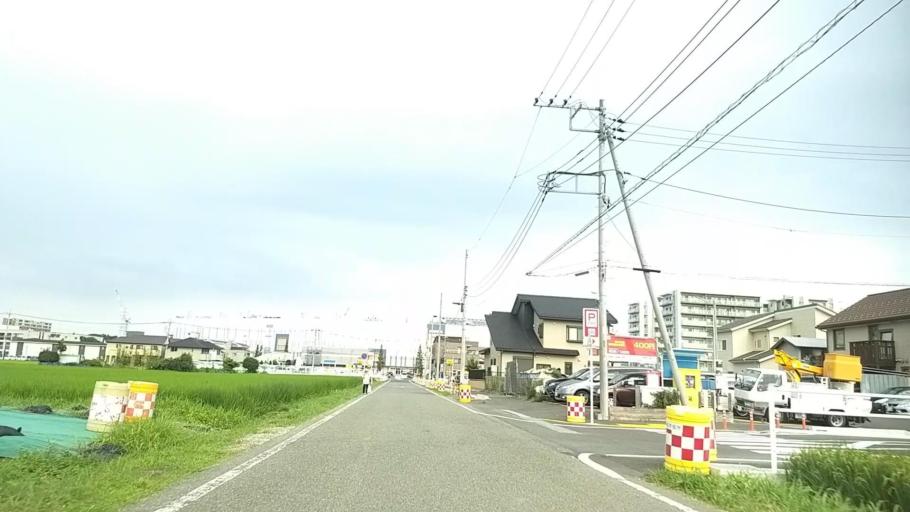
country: JP
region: Kanagawa
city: Atsugi
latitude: 35.4559
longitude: 139.3851
